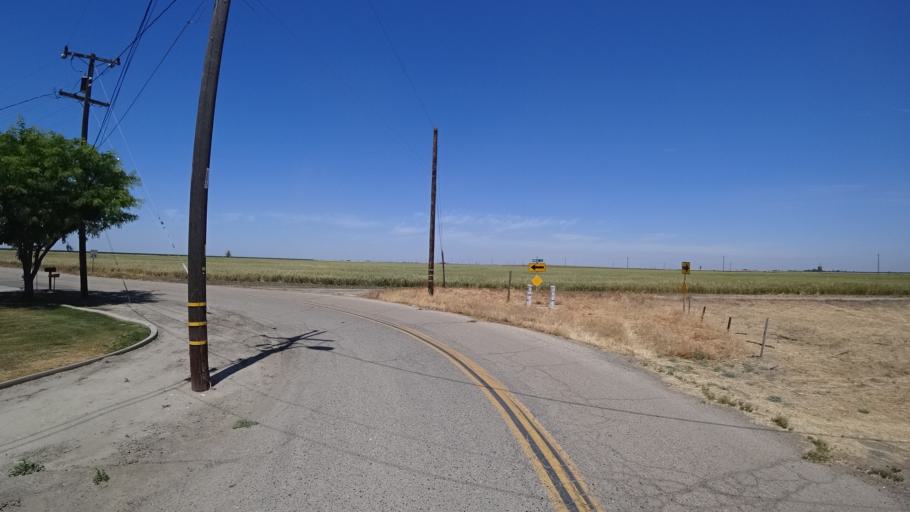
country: US
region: California
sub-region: Kings County
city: Corcoran
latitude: 36.1198
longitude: -119.5768
